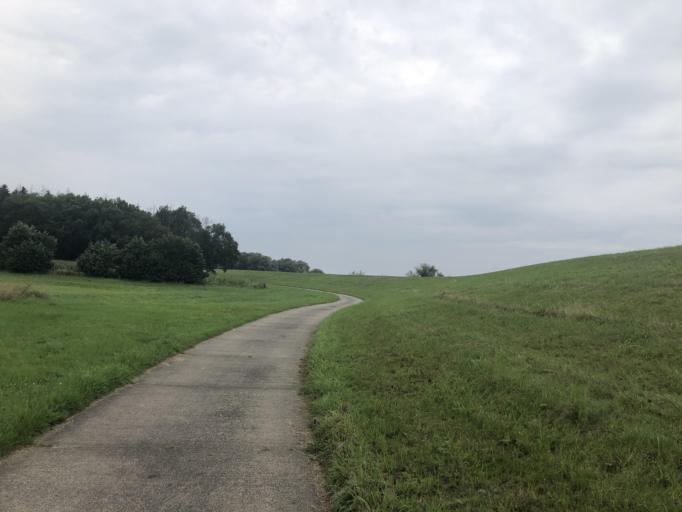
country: DE
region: Mecklenburg-Vorpommern
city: Nostorf
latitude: 53.3612
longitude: 10.6622
